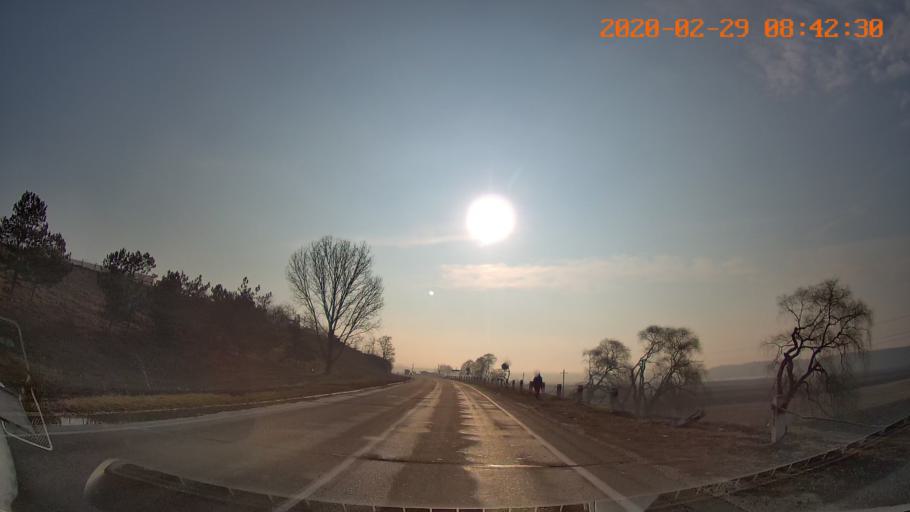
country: MD
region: Anenii Noi
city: Varnita
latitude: 46.9221
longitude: 29.4512
